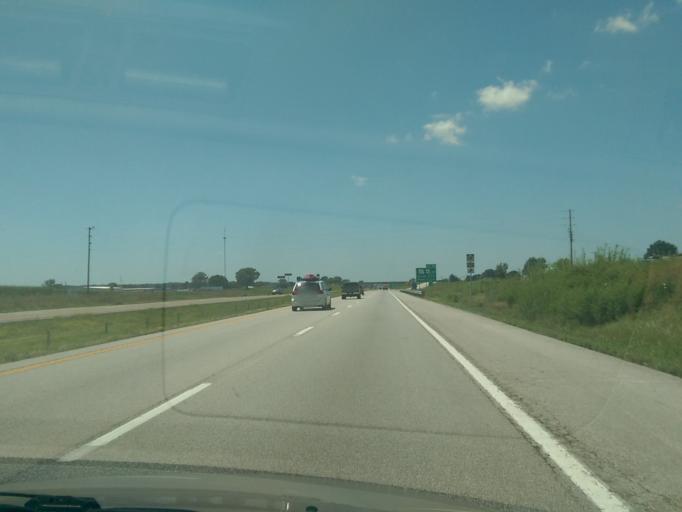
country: US
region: Missouri
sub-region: Cooper County
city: Boonville
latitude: 38.9353
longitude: -92.8399
